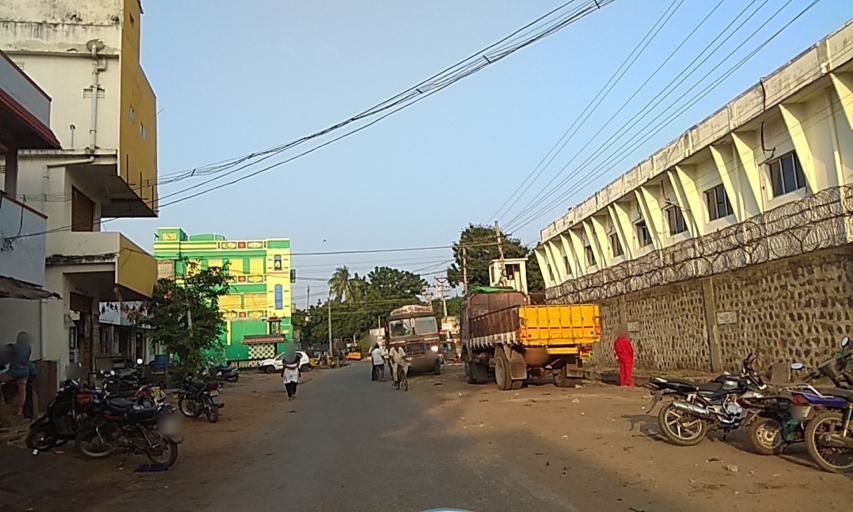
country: IN
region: Andhra Pradesh
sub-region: Krishna
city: Machilipatnam
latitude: 16.1884
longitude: 81.1353
